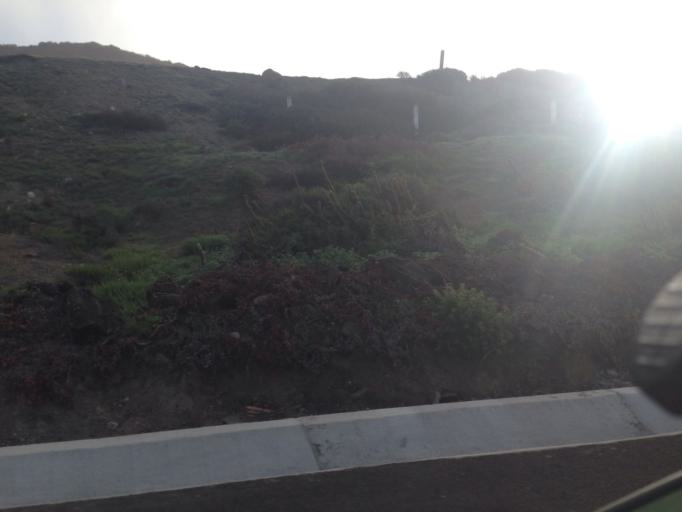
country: MX
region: Baja California
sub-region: Playas de Rosarito
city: Santa Anita
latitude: 32.1269
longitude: -116.8838
